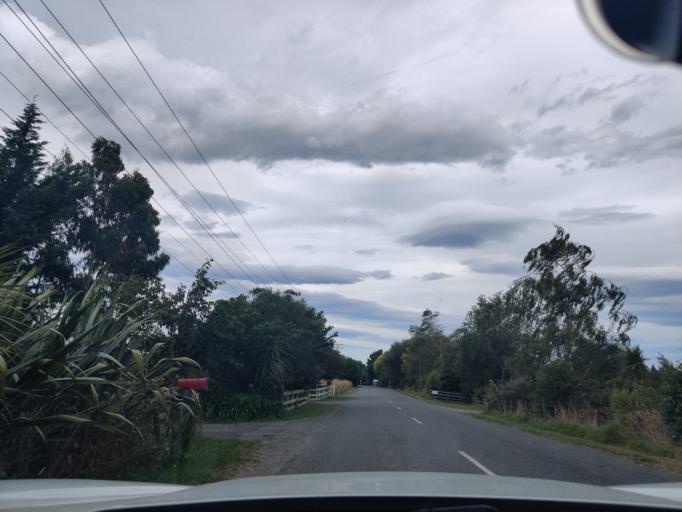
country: NZ
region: Wellington
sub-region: Masterton District
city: Masterton
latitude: -41.0422
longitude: 175.5049
